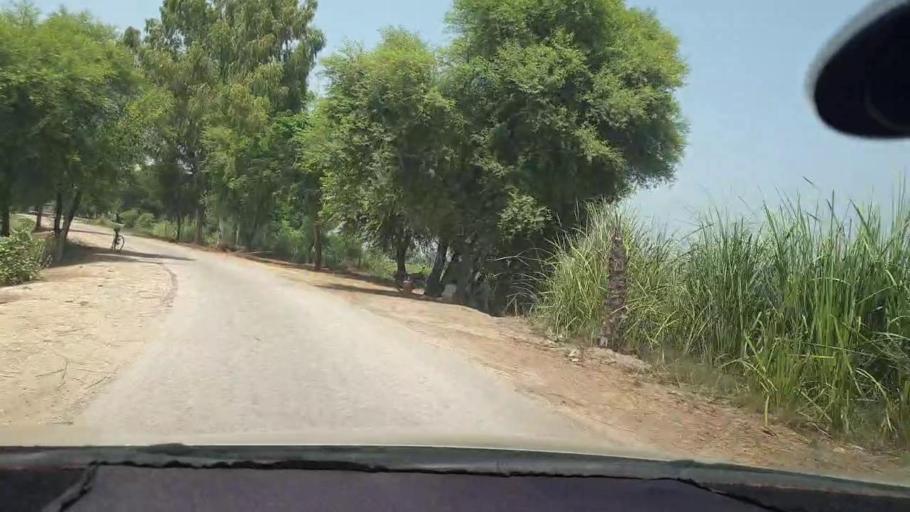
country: PK
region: Sindh
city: Kambar
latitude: 27.6626
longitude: 67.9474
